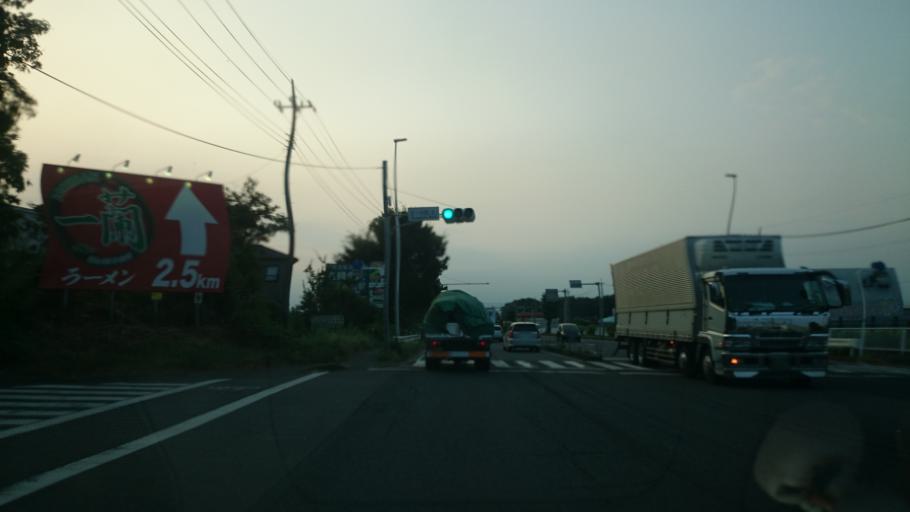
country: JP
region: Saitama
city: Iwatsuki
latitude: 35.9441
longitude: 139.6752
